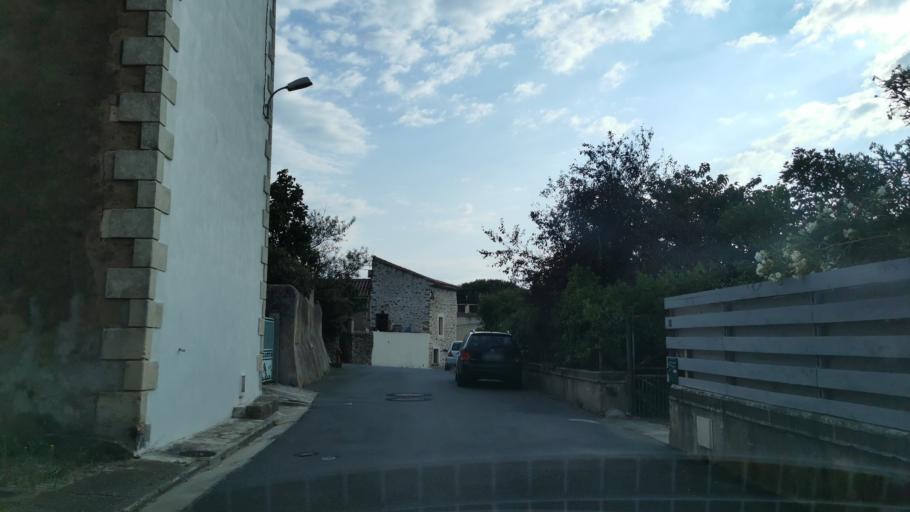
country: FR
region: Languedoc-Roussillon
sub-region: Departement de l'Aude
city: Bizanet
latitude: 43.1643
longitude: 2.8718
